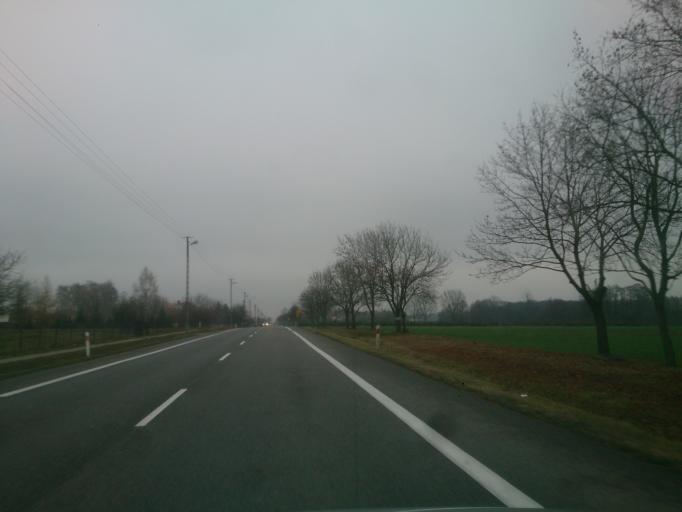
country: PL
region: Masovian Voivodeship
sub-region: Powiat plonski
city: Dzierzaznia
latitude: 52.6287
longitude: 20.2130
